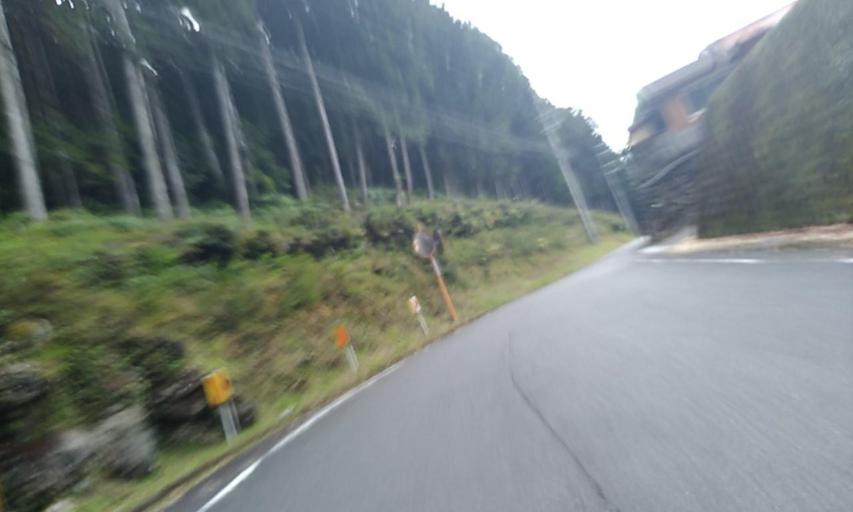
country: JP
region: Wakayama
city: Shingu
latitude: 33.9323
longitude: 135.9795
